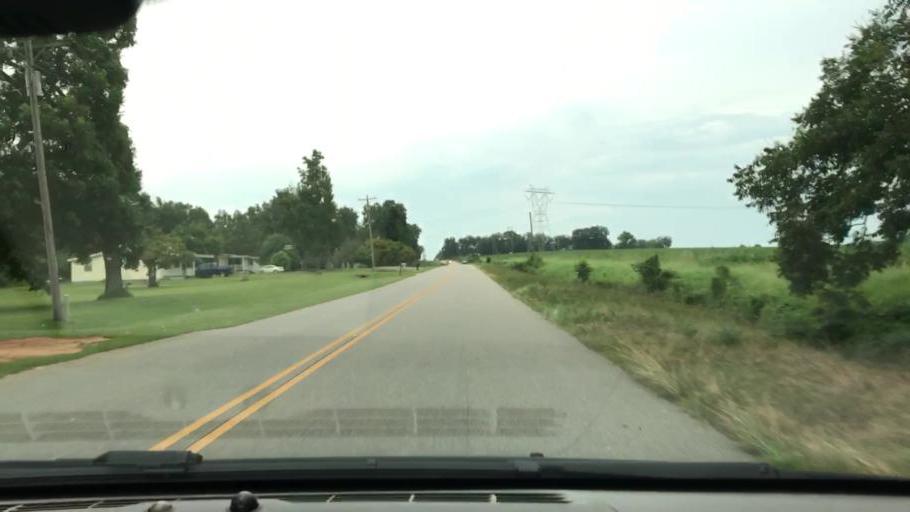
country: US
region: Alabama
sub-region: Houston County
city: Webb
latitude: 31.2703
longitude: -85.1668
